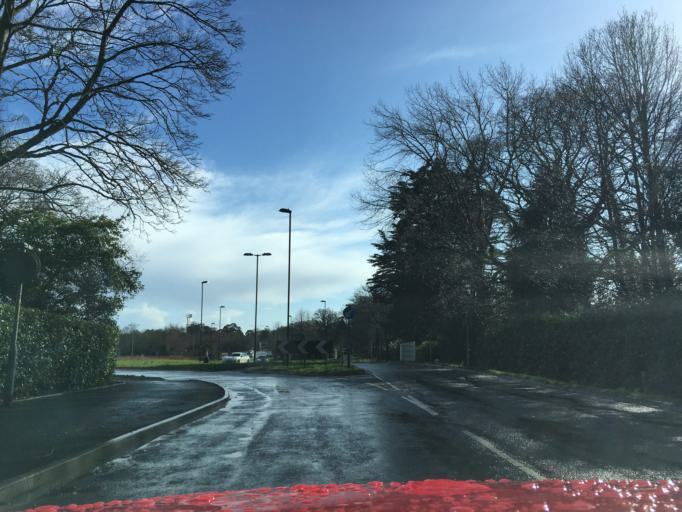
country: GB
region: England
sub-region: Southampton
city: Southampton
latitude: 50.9556
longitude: -1.4042
